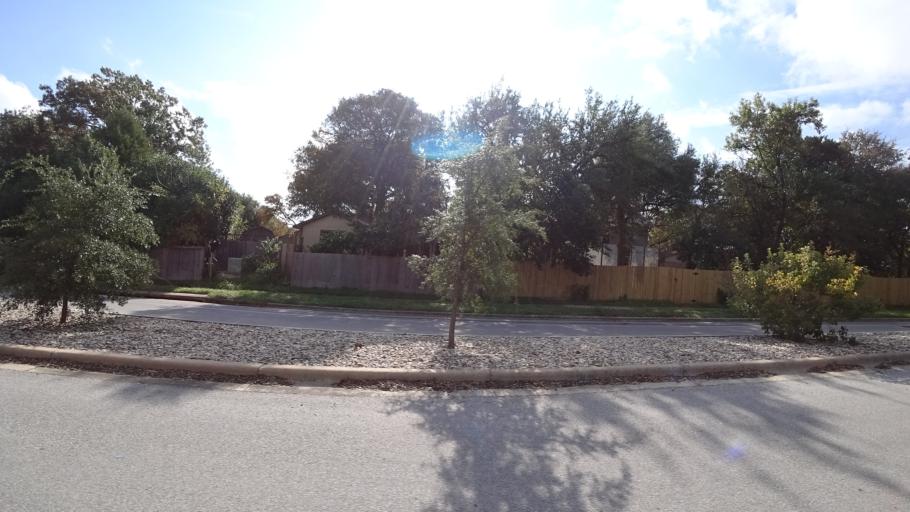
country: US
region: Texas
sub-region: Travis County
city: Shady Hollow
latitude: 30.1903
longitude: -97.8299
